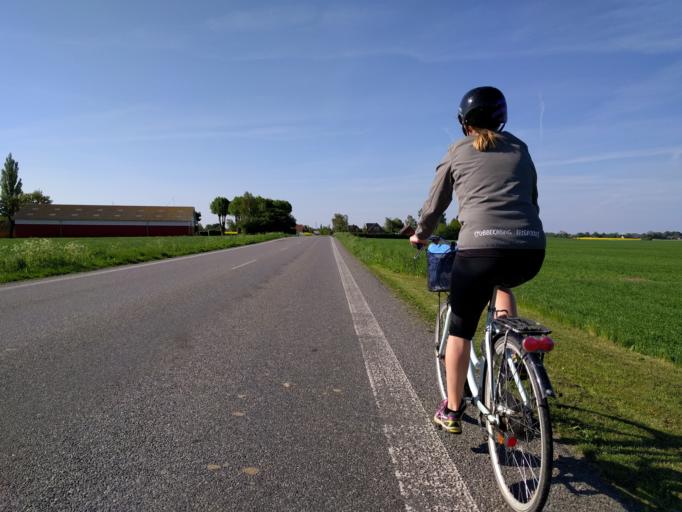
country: DK
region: Zealand
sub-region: Guldborgsund Kommune
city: Stubbekobing
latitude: 54.8139
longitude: 11.9930
